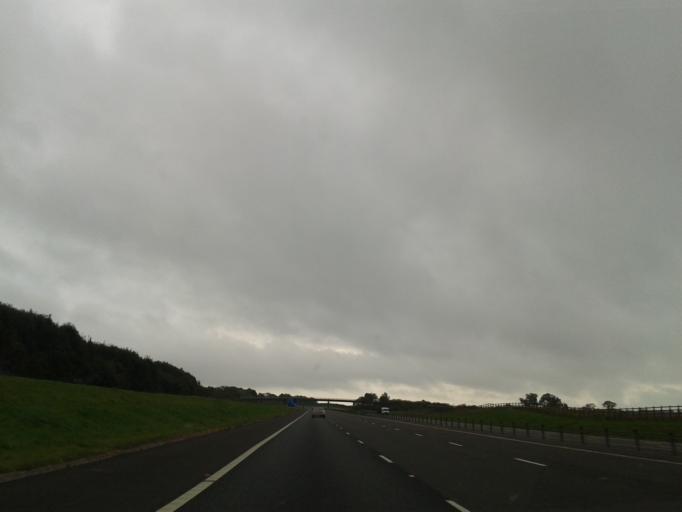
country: GB
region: Scotland
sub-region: Dumfries and Galloway
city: Lockerbie
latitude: 55.1544
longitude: -3.3837
